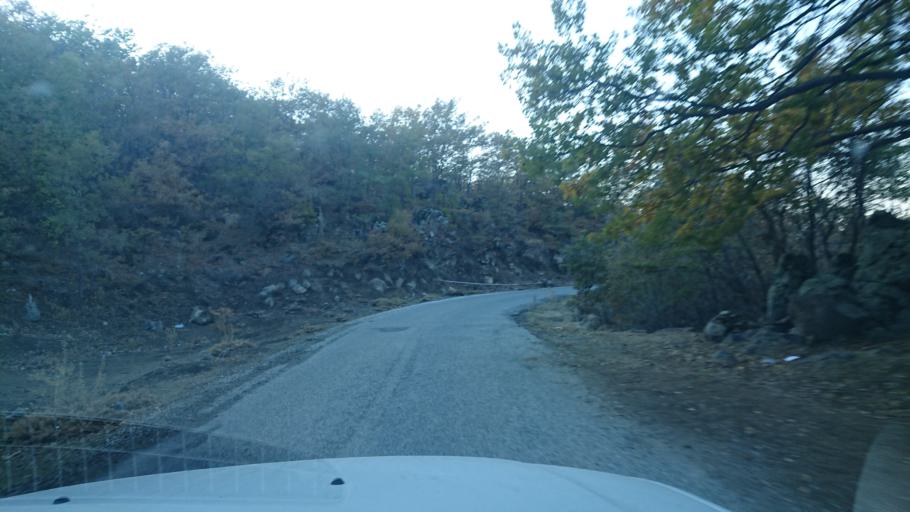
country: TR
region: Aksaray
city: Taspinar
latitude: 38.1658
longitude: 34.1967
